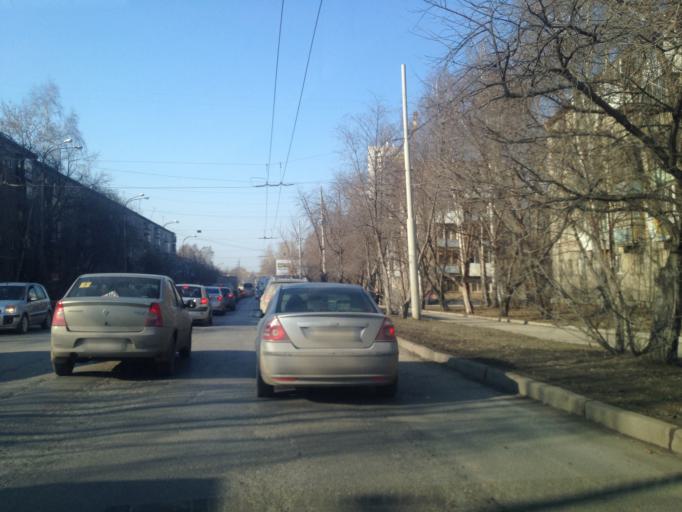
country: RU
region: Sverdlovsk
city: Yekaterinburg
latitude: 56.8587
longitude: 60.6537
